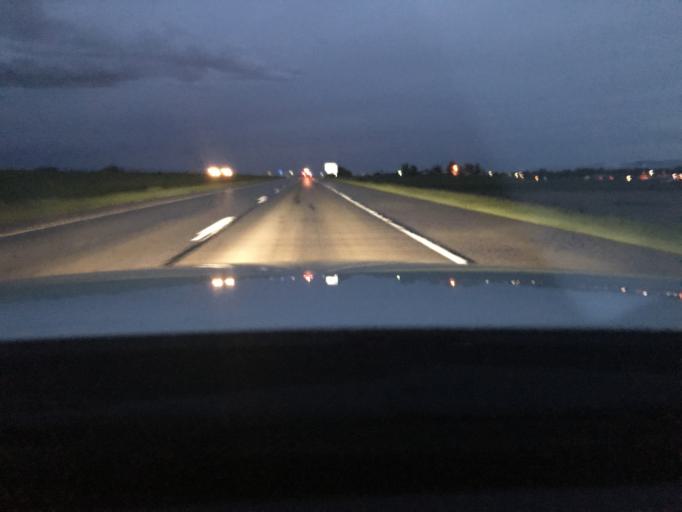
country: US
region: Colorado
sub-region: Larimer County
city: Wellington
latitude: 40.7168
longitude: -104.9942
